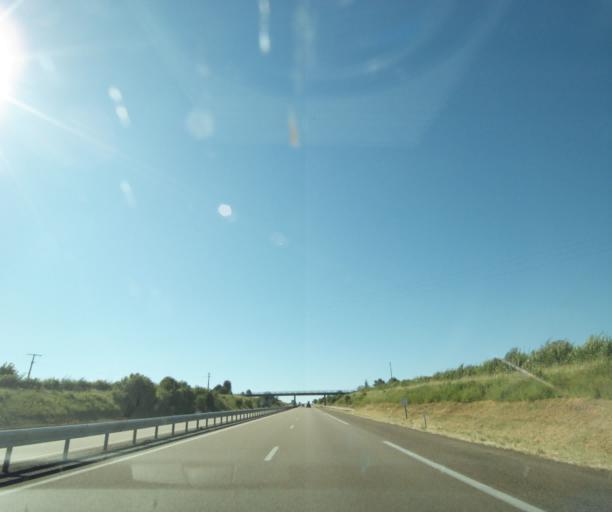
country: FR
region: Champagne-Ardenne
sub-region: Departement de la Haute-Marne
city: Chamarandes-Choignes
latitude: 47.9800
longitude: 5.1334
